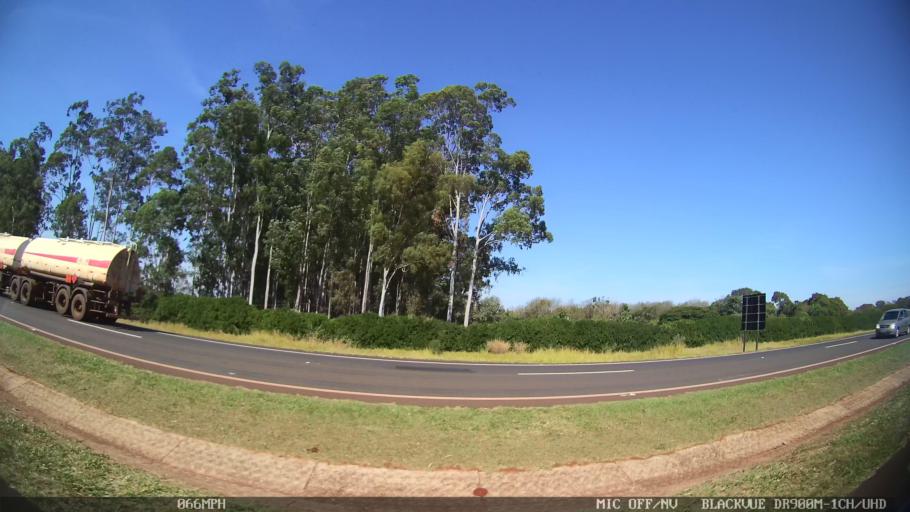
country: BR
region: Sao Paulo
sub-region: Ribeirao Preto
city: Ribeirao Preto
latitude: -21.1234
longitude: -47.8387
